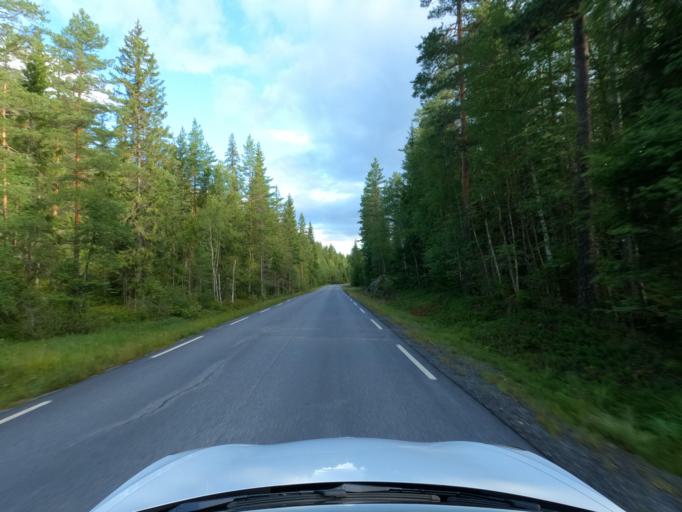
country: NO
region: Telemark
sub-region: Hjartdal
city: Sauland
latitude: 59.7760
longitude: 9.0958
